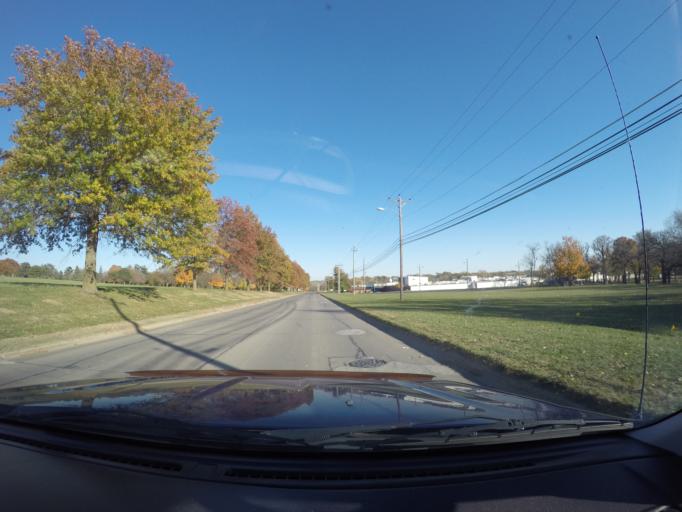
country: US
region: Nebraska
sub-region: Otoe County
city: Nebraska City
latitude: 40.6677
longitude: -95.8771
